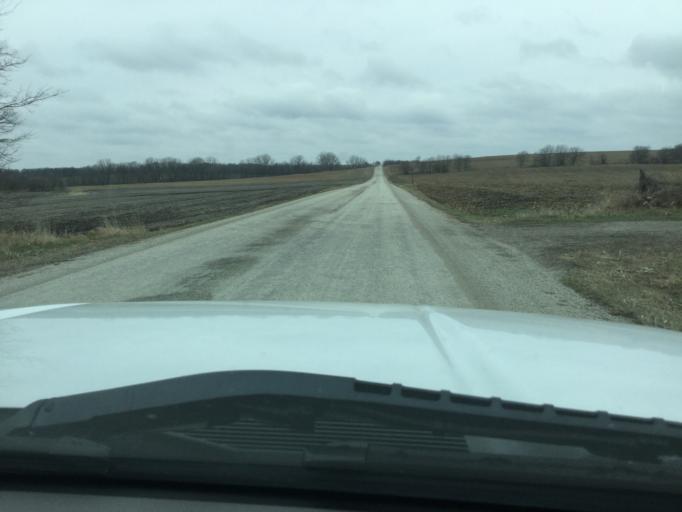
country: US
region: Kansas
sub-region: Nemaha County
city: Sabetha
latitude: 39.7979
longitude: -95.7376
